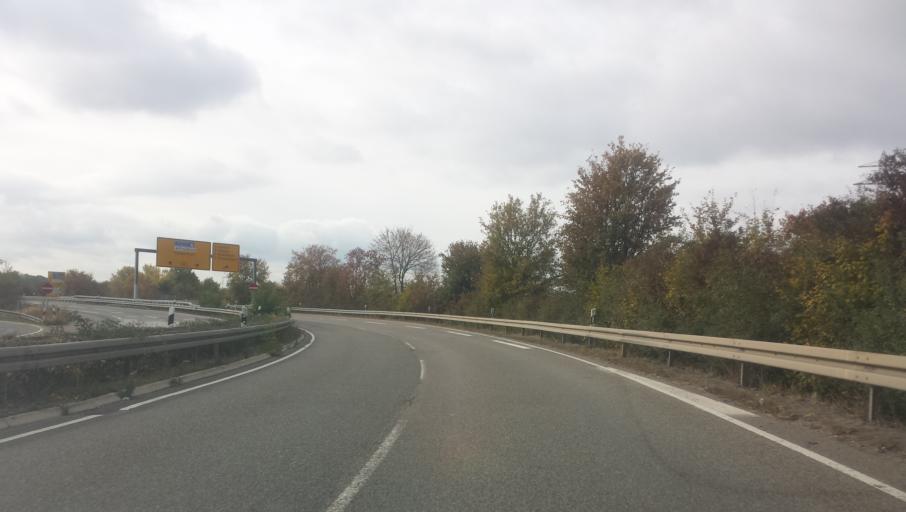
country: DE
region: Hesse
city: Kelsterbach
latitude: 50.0775
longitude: 8.5441
